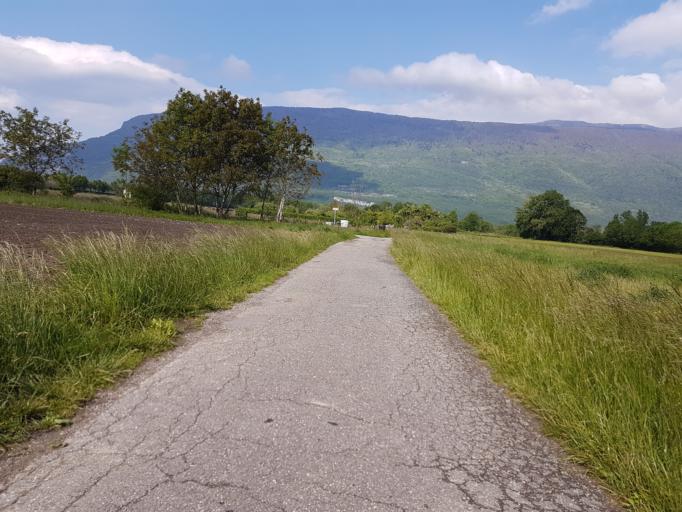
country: FR
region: Rhone-Alpes
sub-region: Departement de la Savoie
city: Chindrieux
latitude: 45.8897
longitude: 5.8409
